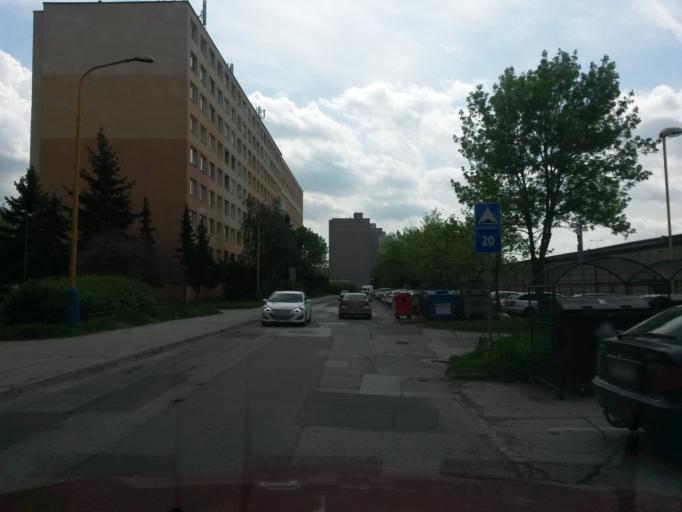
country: SK
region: Kosicky
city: Kosice
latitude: 48.7074
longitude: 21.2492
